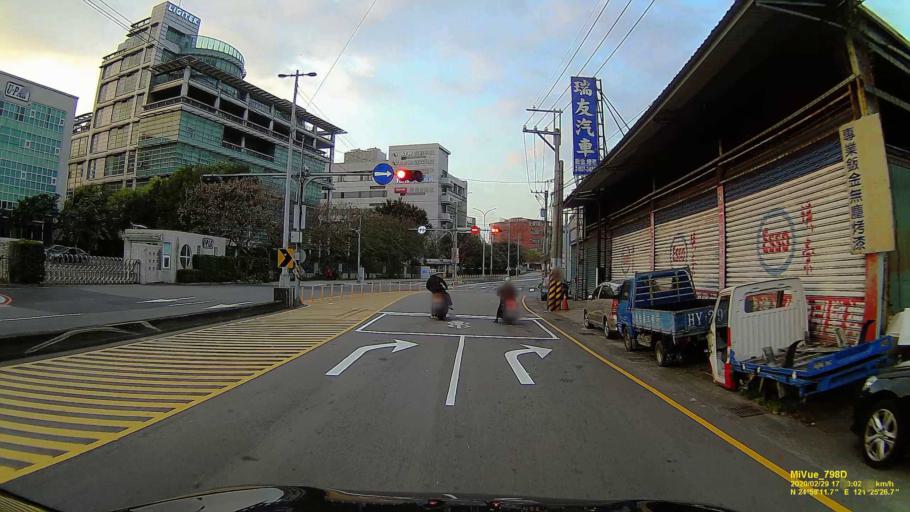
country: TW
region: Taipei
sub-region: Taipei
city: Banqiao
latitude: 24.9867
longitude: 121.4240
